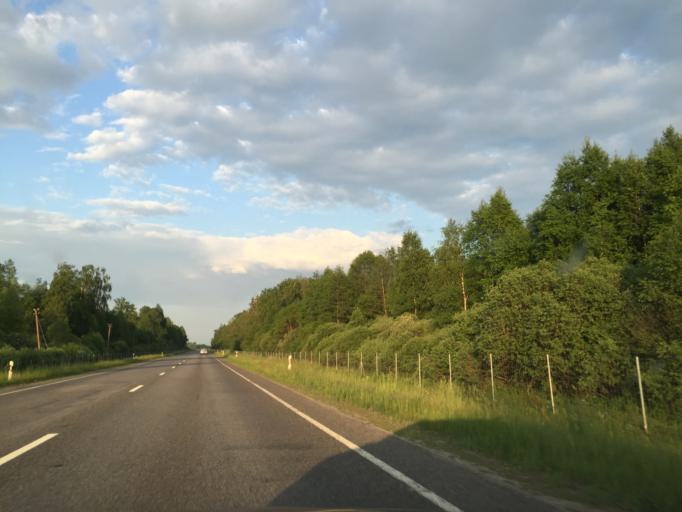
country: LT
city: Kursenai
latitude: 55.9996
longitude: 22.8232
